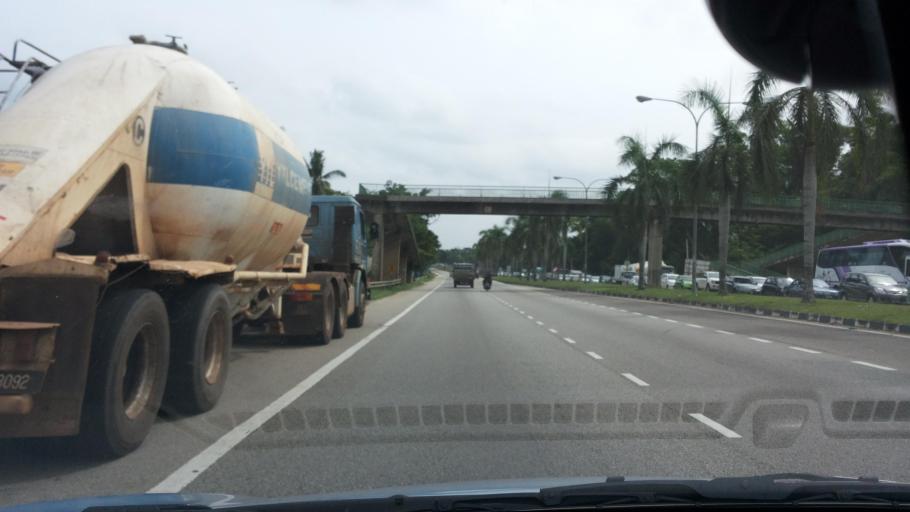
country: MY
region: Pahang
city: Kuantan
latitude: 3.7543
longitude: 103.1994
